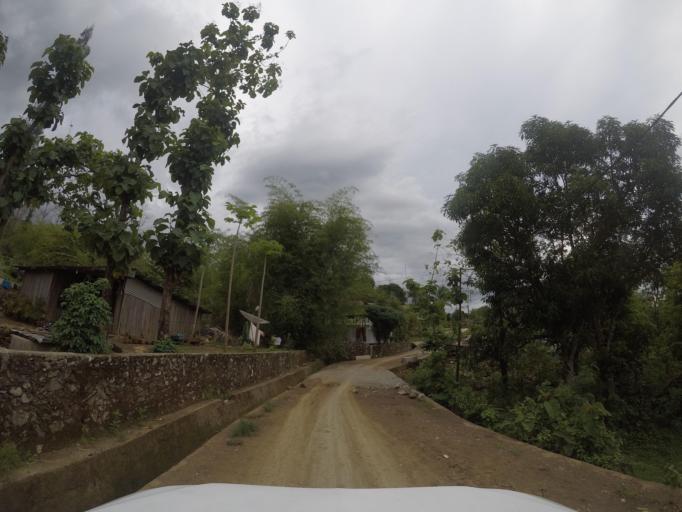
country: TL
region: Bobonaro
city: Maliana
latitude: -8.9941
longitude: 125.2160
